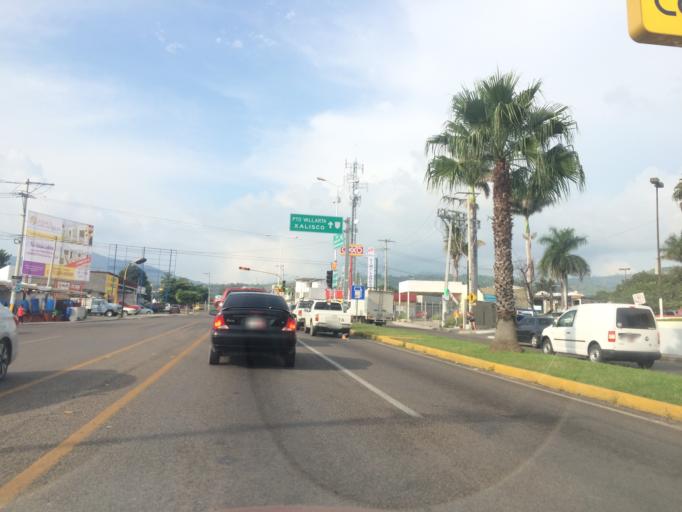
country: MX
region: Nayarit
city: Xalisco
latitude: 21.4520
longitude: -104.8985
